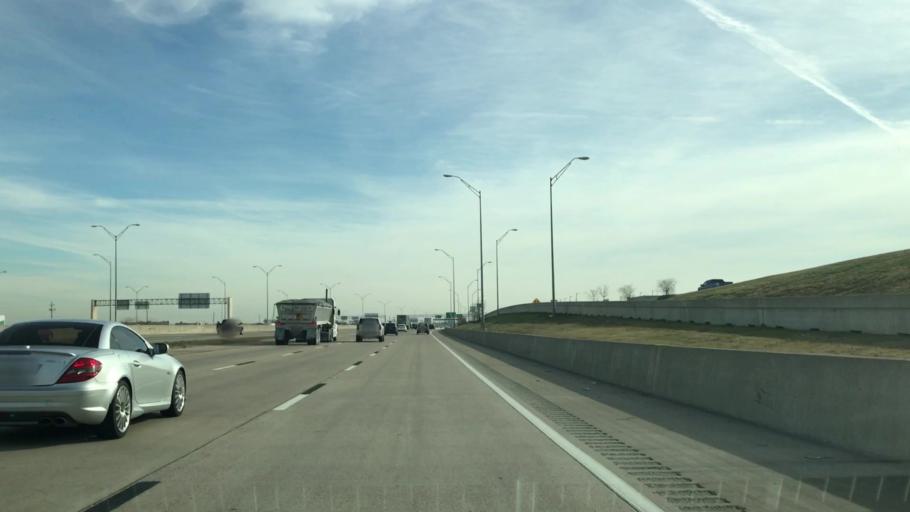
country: US
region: Texas
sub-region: Tarrant County
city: Grapevine
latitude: 32.9226
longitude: -97.0771
